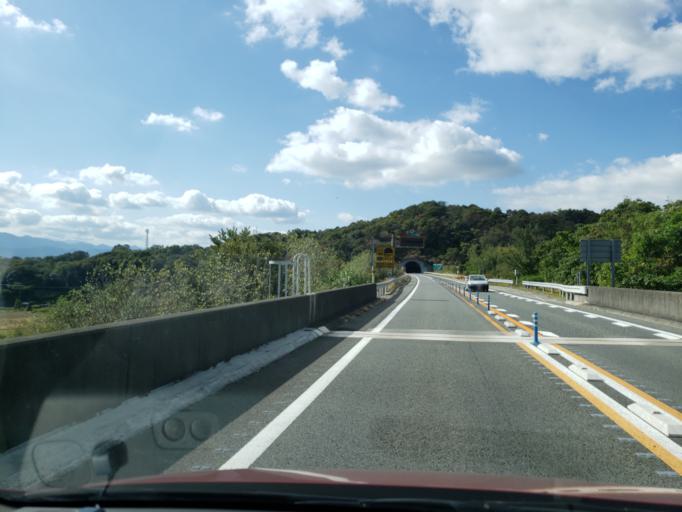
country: JP
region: Tokushima
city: Kamojimacho-jogejima
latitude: 34.1165
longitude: 134.3263
